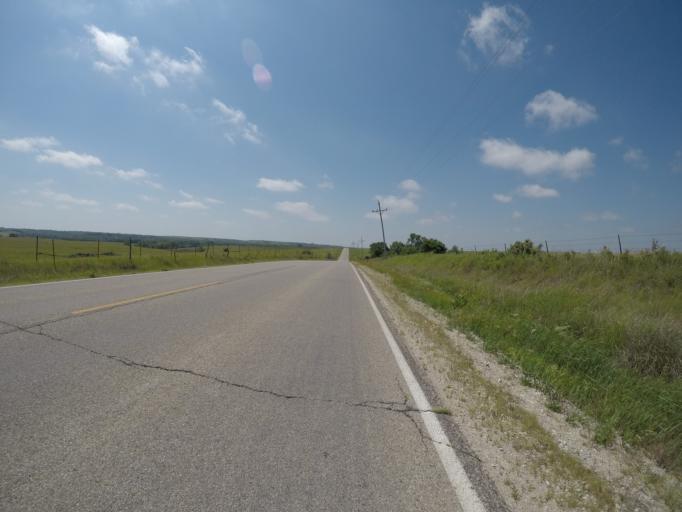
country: US
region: Kansas
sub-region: Pottawatomie County
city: Westmoreland
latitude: 39.3822
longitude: -96.4267
